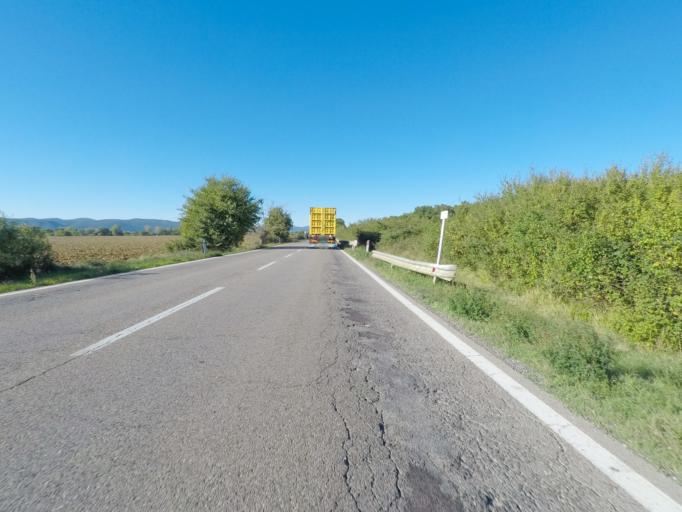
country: IT
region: Tuscany
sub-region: Provincia di Siena
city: Rosia
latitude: 43.2125
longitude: 11.2779
